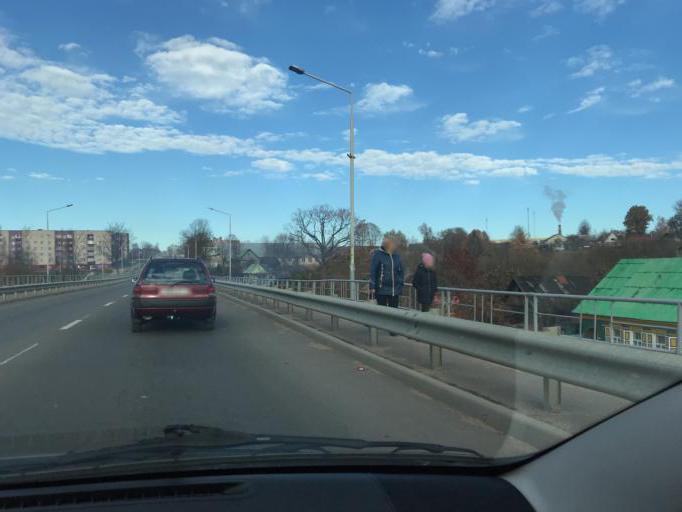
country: BY
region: Vitebsk
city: Haradok
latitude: 55.4670
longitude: 29.9768
